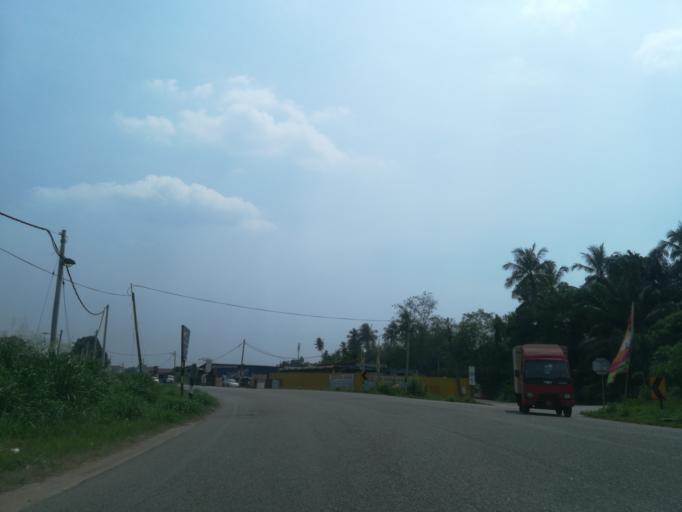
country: MY
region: Penang
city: Tasek Glugor
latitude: 5.4355
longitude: 100.5371
